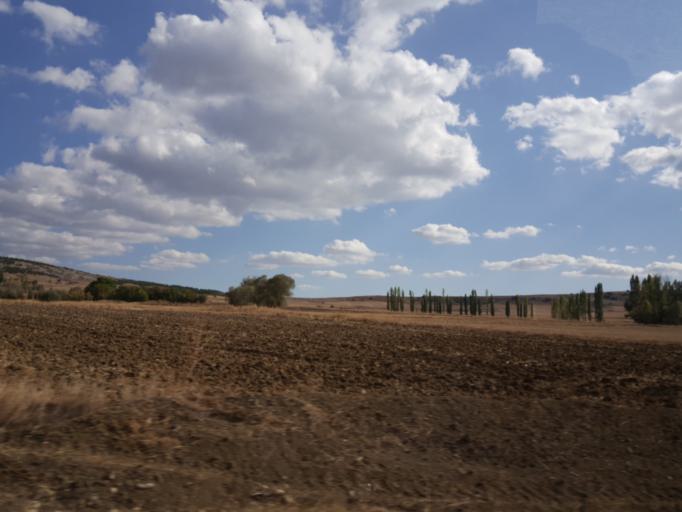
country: TR
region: Tokat
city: Sulusaray
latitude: 39.9874
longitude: 35.9805
